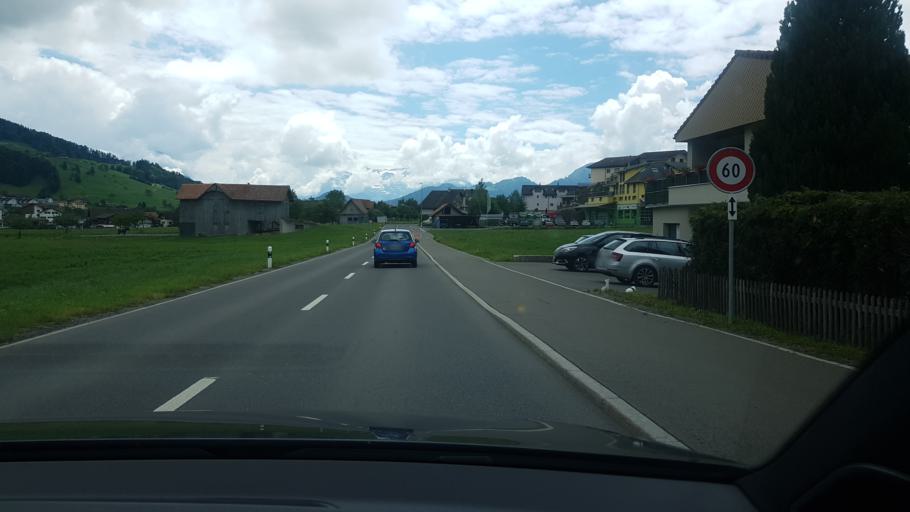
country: CH
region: Schwyz
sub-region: Bezirk Schwyz
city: Sattel
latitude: 47.0859
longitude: 8.6299
